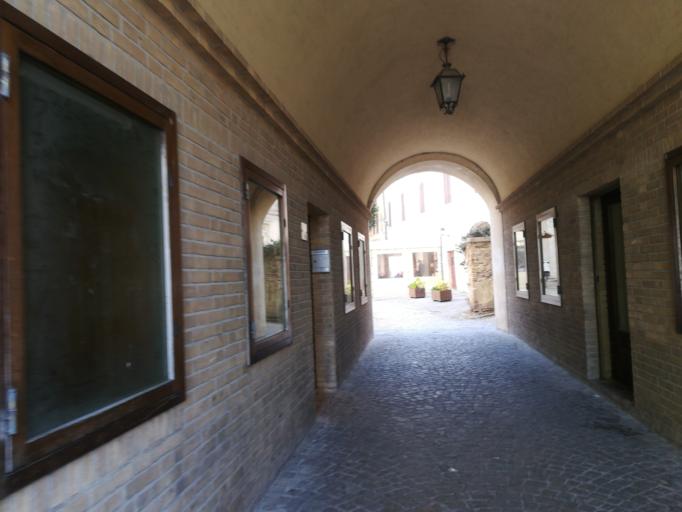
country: IT
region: The Marches
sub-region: Provincia di Macerata
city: Cingoli
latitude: 43.3752
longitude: 13.2151
